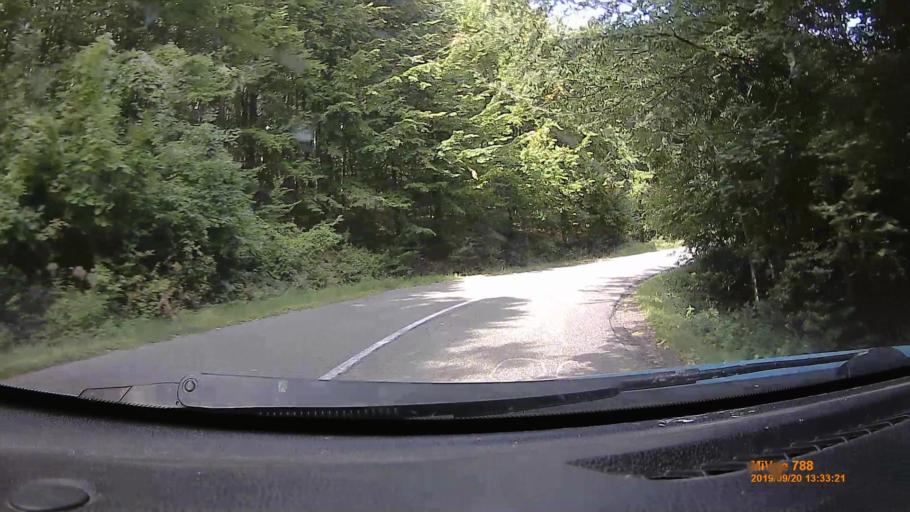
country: HU
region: Heves
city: Szilvasvarad
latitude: 48.0573
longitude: 20.4997
